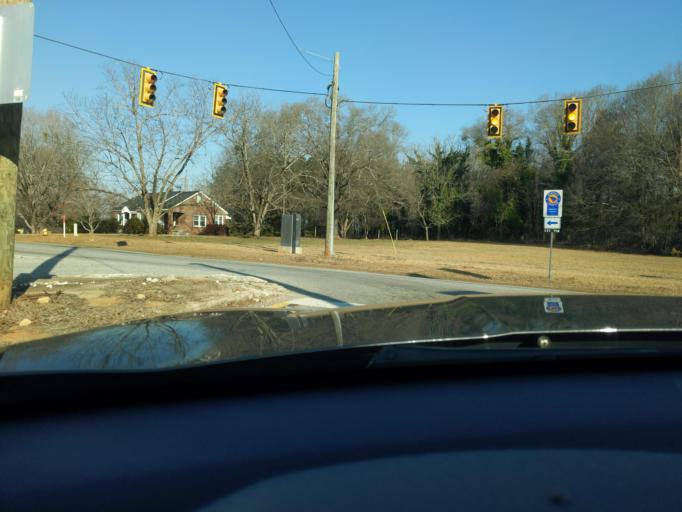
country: US
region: South Carolina
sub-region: Greenwood County
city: Greenwood
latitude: 34.1954
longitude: -82.1306
